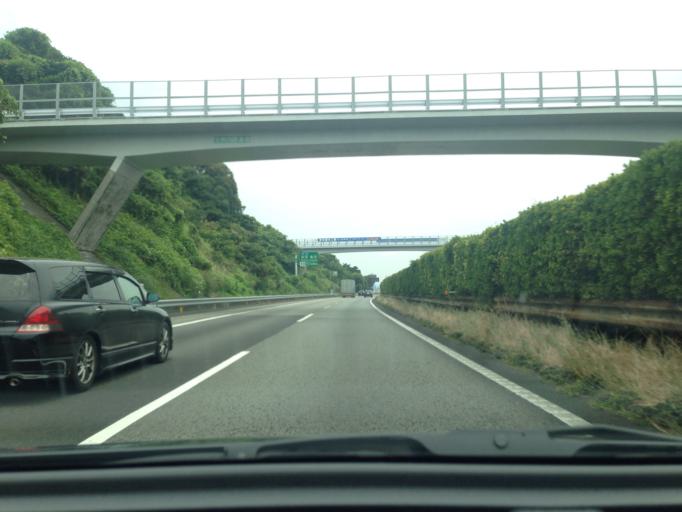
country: JP
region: Shizuoka
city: Shimada
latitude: 34.7836
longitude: 138.2299
